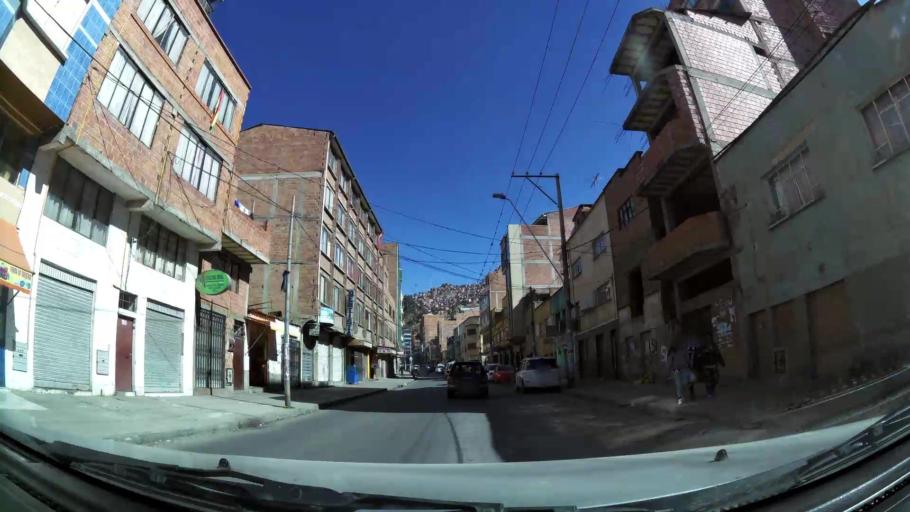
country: BO
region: La Paz
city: La Paz
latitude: -16.5081
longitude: -68.1431
